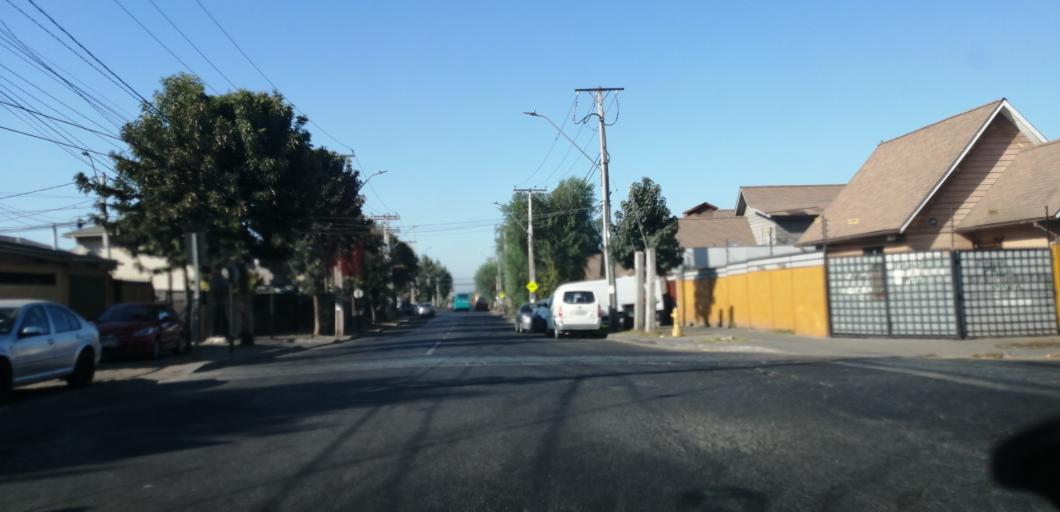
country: CL
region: Santiago Metropolitan
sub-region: Provincia de Santiago
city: Lo Prado
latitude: -33.4334
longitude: -70.7749
